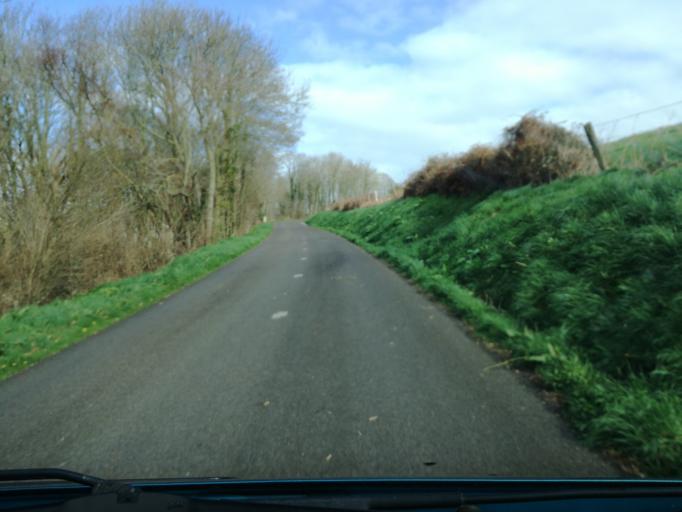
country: FR
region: Haute-Normandie
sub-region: Departement de la Seine-Maritime
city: Yport
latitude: 49.7355
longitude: 0.3205
